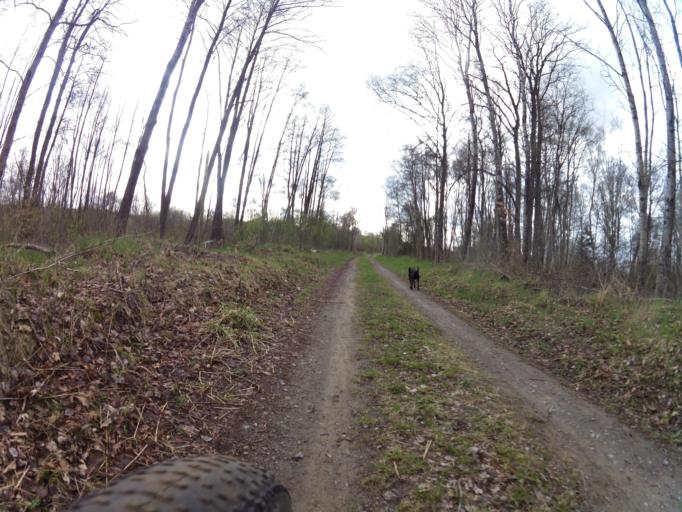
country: PL
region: West Pomeranian Voivodeship
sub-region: Powiat slawienski
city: Slawno
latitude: 54.3305
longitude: 16.7300
